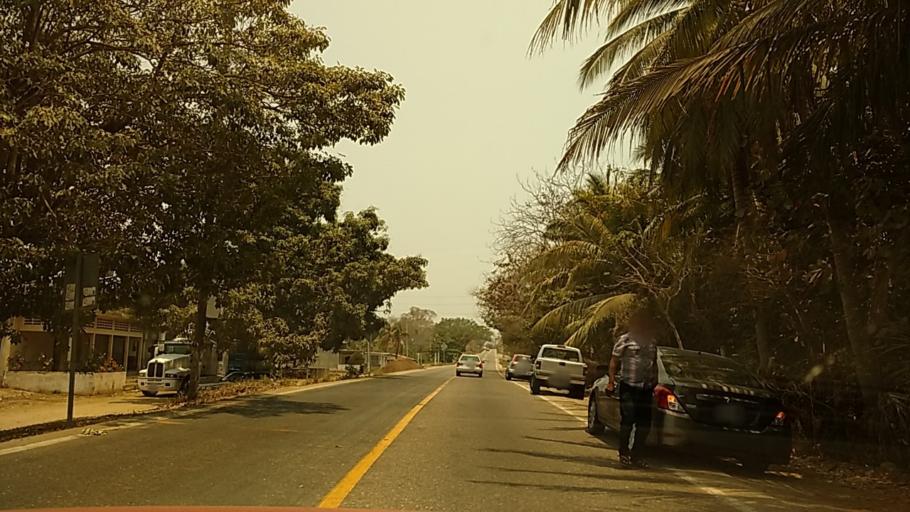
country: MX
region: Guerrero
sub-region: Coyuca de Benitez
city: El Espinalillo
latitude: 17.0058
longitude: -100.1950
